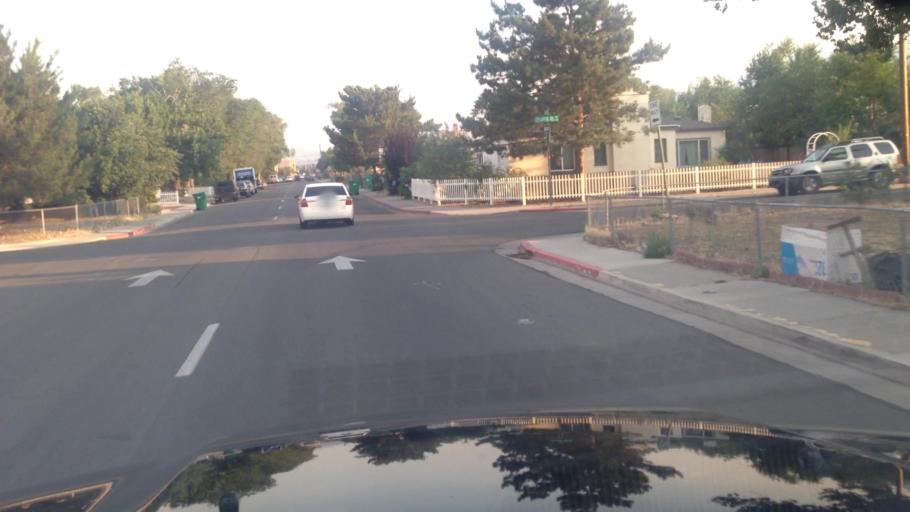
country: US
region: Nevada
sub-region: Washoe County
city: Reno
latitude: 39.5108
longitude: -119.7982
